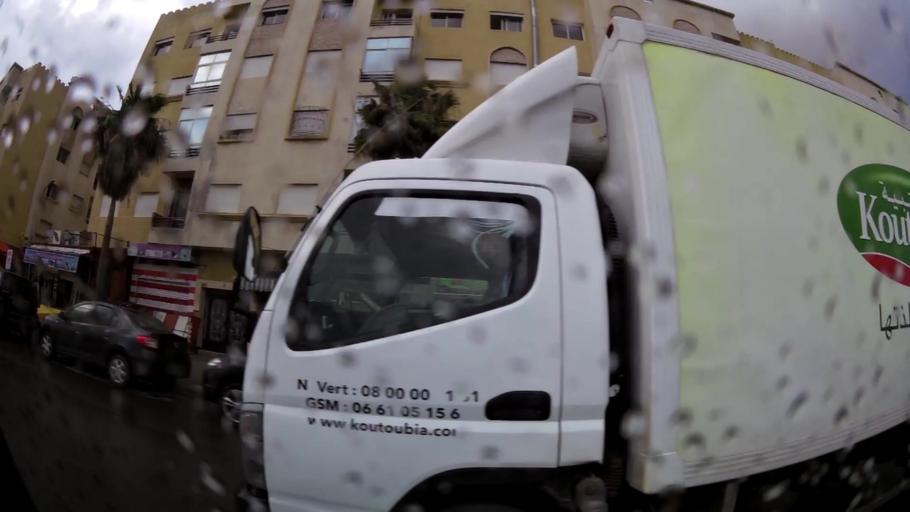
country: MA
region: Grand Casablanca
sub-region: Mohammedia
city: Mohammedia
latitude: 33.6788
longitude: -7.4004
